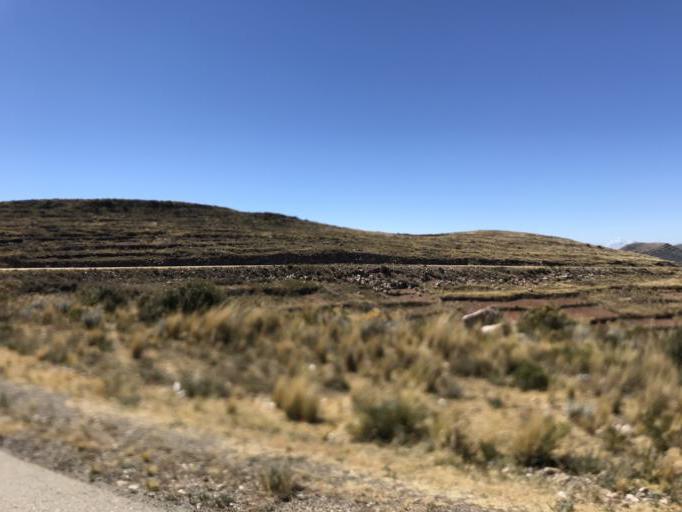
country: BO
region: La Paz
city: San Pedro
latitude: -16.1866
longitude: -68.9662
